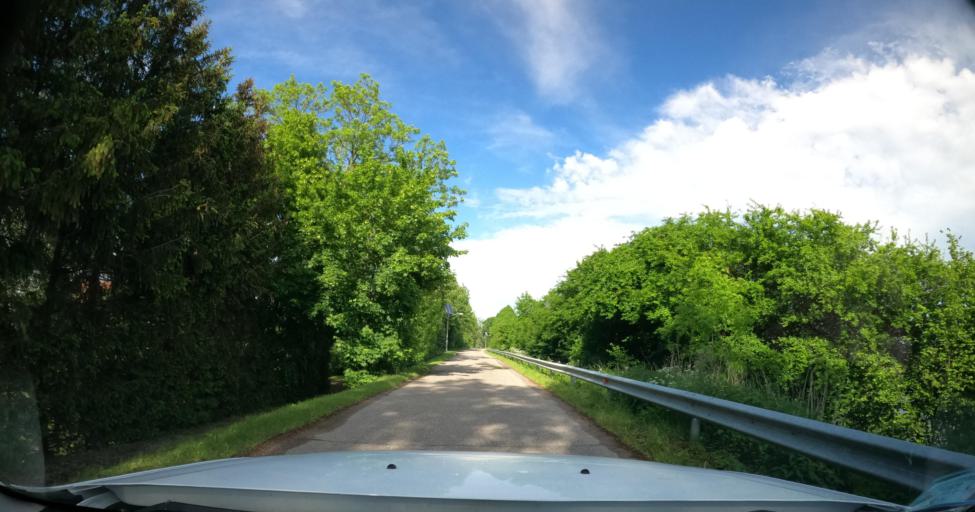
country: PL
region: Warmian-Masurian Voivodeship
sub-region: Powiat elblaski
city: Gronowo Elblaskie
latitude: 54.1781
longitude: 19.2626
